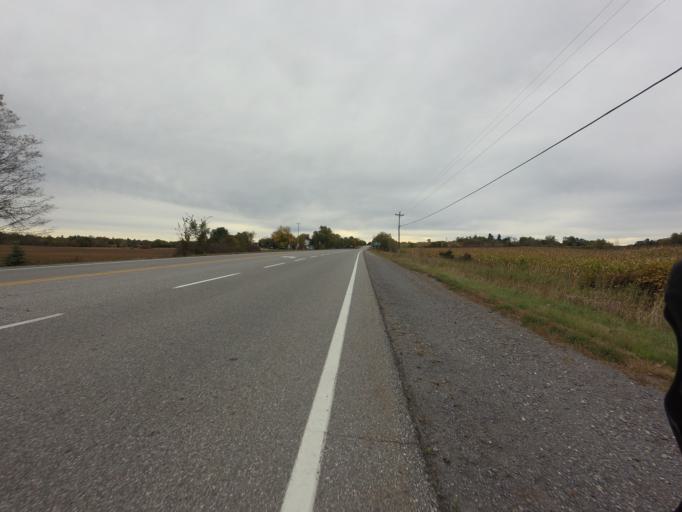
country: CA
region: Ontario
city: Gananoque
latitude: 44.4711
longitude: -76.2434
